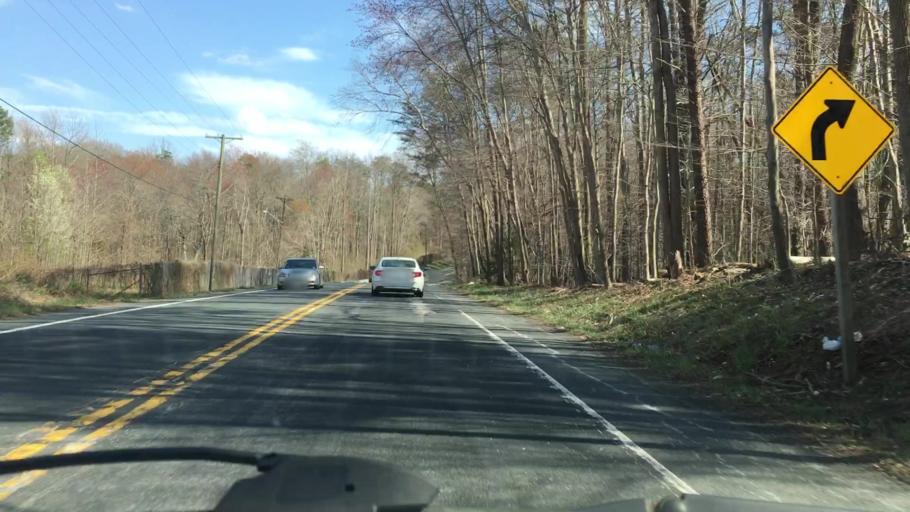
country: US
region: Maryland
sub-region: Anne Arundel County
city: Maryland City
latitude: 39.0421
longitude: -76.7972
